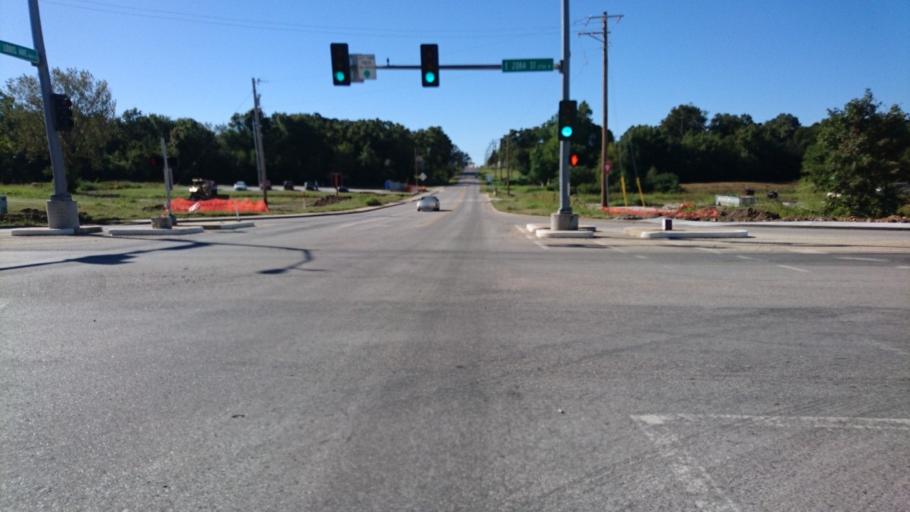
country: US
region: Missouri
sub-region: Jasper County
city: Joplin
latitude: 37.1133
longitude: -94.4941
